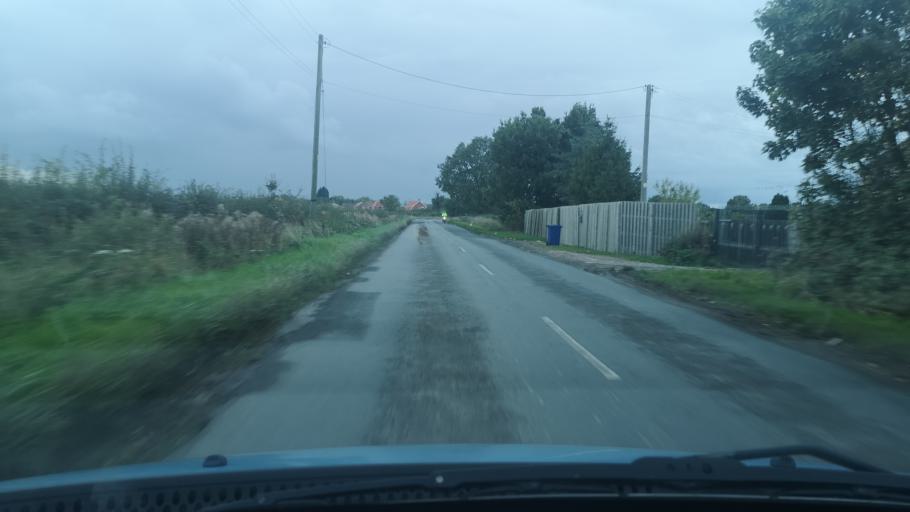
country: GB
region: England
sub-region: Doncaster
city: Moss
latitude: 53.6232
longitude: -1.0870
